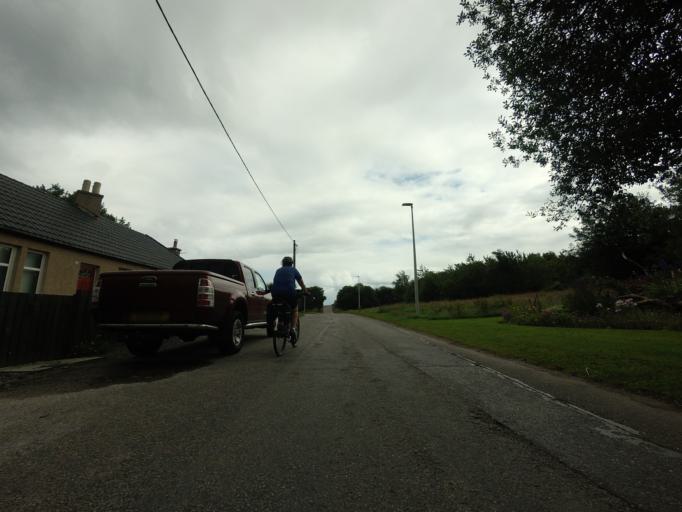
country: GB
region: Scotland
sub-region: Moray
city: Fochabers
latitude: 57.6620
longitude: -3.1150
